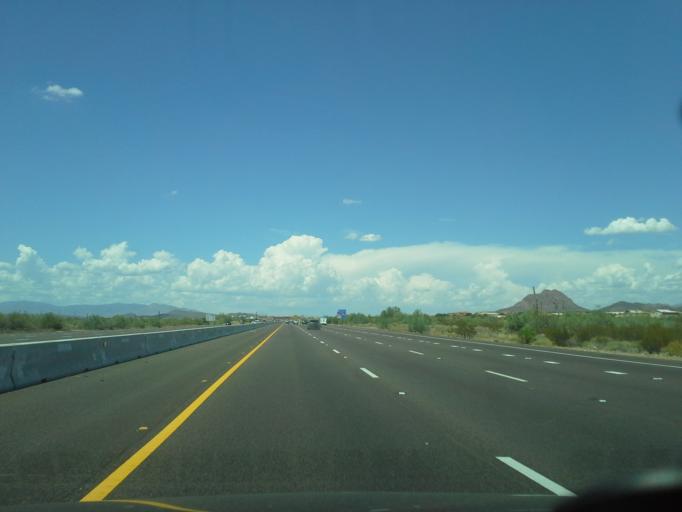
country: US
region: Arizona
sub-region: Maricopa County
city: Anthem
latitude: 33.8520
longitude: -112.1439
